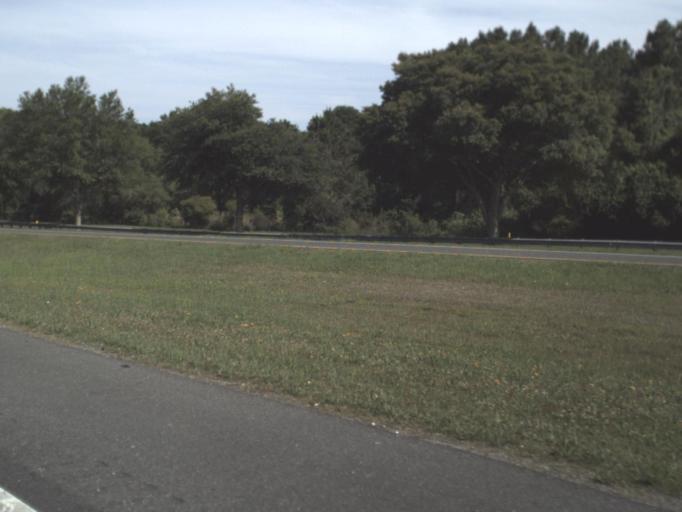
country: US
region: Florida
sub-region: Saint Johns County
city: Ponte Vedra Beach
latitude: 30.2515
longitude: -81.4945
